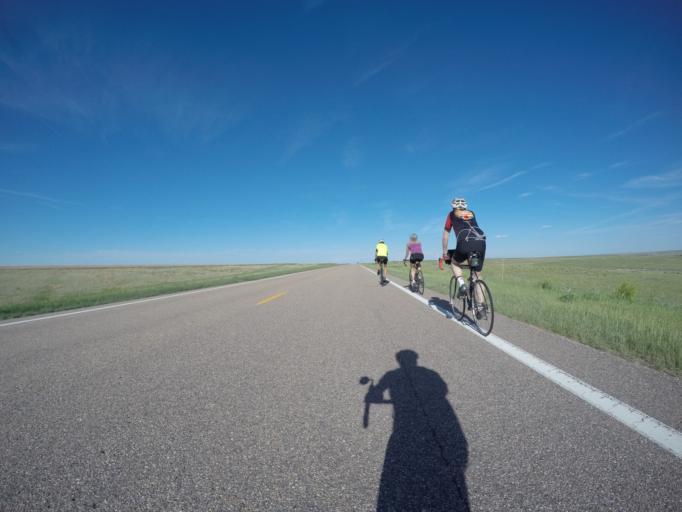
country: US
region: Kansas
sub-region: Cheyenne County
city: Saint Francis
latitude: 39.7570
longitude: -101.8942
